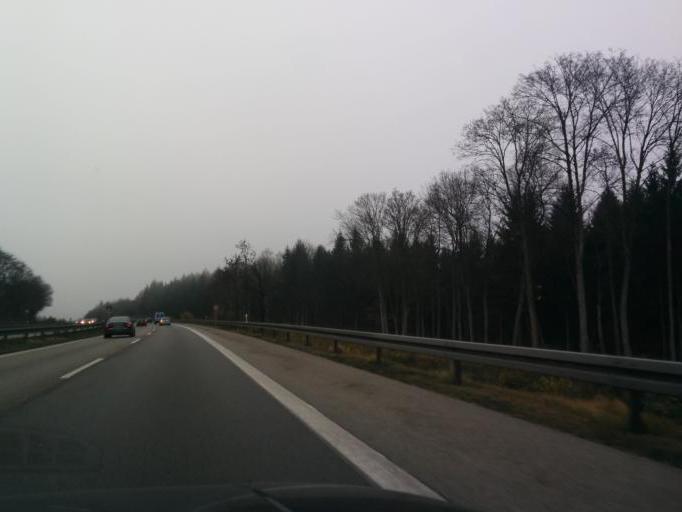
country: DE
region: Bavaria
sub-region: Upper Bavaria
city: Wessling
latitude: 48.0921
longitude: 11.2626
